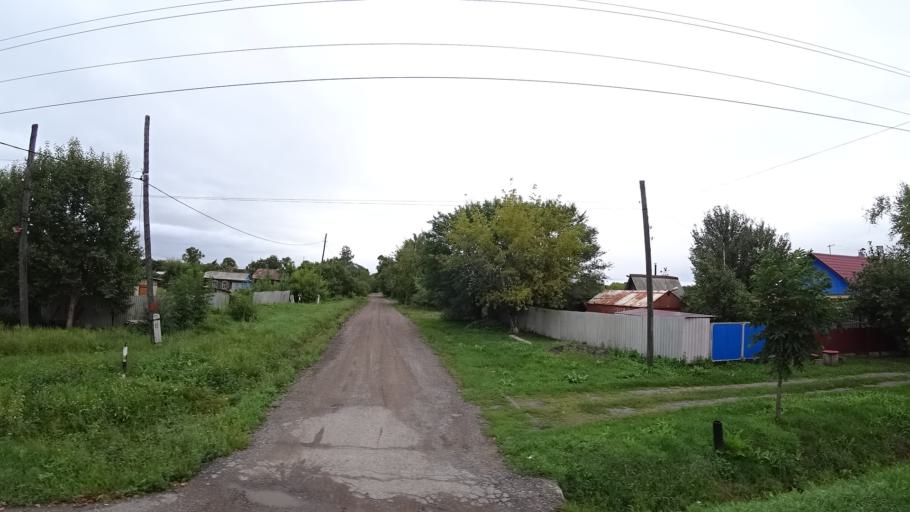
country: RU
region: Primorskiy
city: Chernigovka
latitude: 44.3428
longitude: 132.5852
